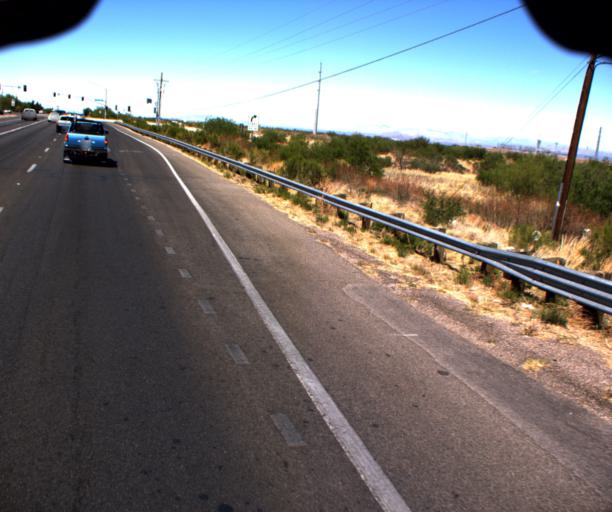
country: US
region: Arizona
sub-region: Cochise County
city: Sierra Vista
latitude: 31.5092
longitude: -110.2573
